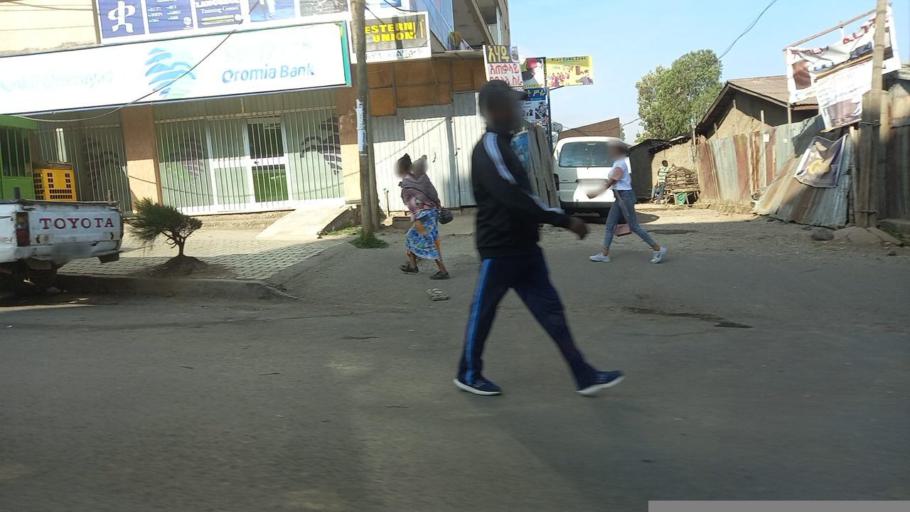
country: ET
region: Adis Abeba
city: Addis Ababa
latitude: 8.9333
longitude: 38.7436
